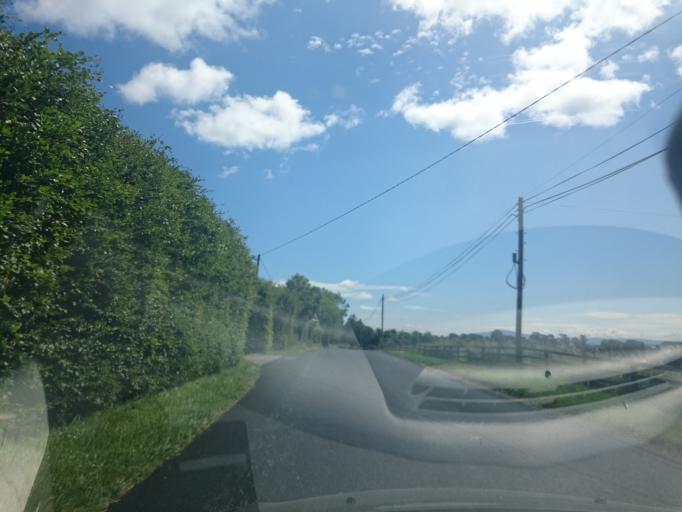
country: IE
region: Leinster
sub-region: Kilkenny
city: Thomastown
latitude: 52.6461
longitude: -7.1204
